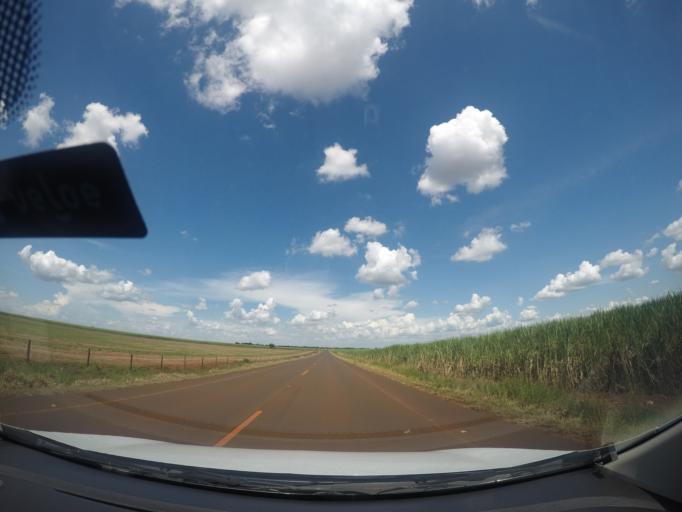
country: BR
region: Minas Gerais
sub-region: Conceicao Das Alagoas
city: Conceicao das Alagoas
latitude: -19.9239
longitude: -48.6718
